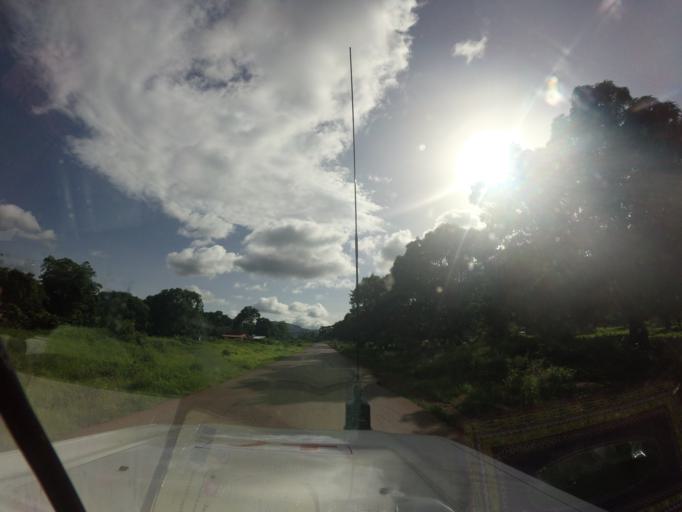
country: GN
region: Kindia
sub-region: Kindia
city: Kindia
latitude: 10.1768
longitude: -12.5082
